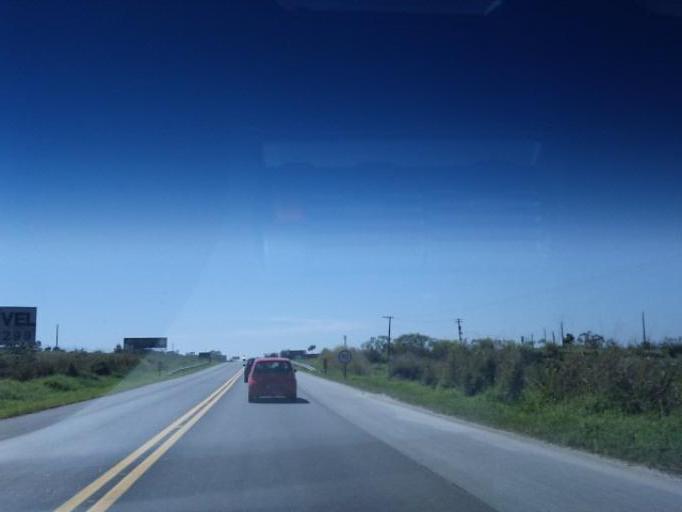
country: BR
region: Sao Paulo
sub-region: Tremembe
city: Tremembe
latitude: -22.9502
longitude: -45.6150
